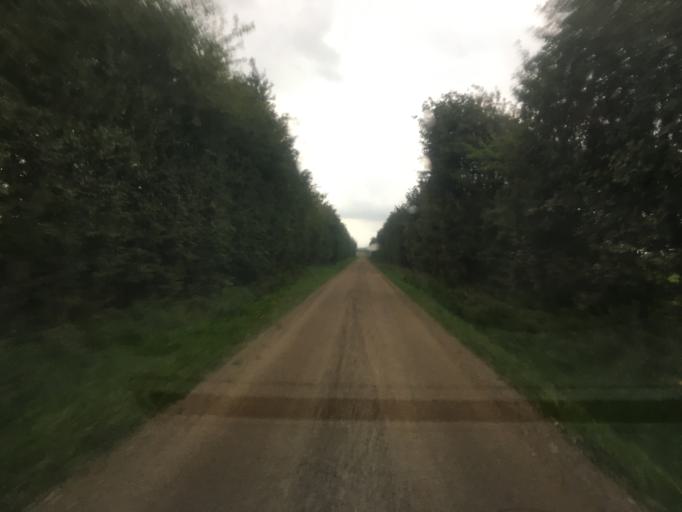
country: DK
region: South Denmark
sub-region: Tonder Kommune
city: Logumkloster
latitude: 54.9727
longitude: 9.0244
